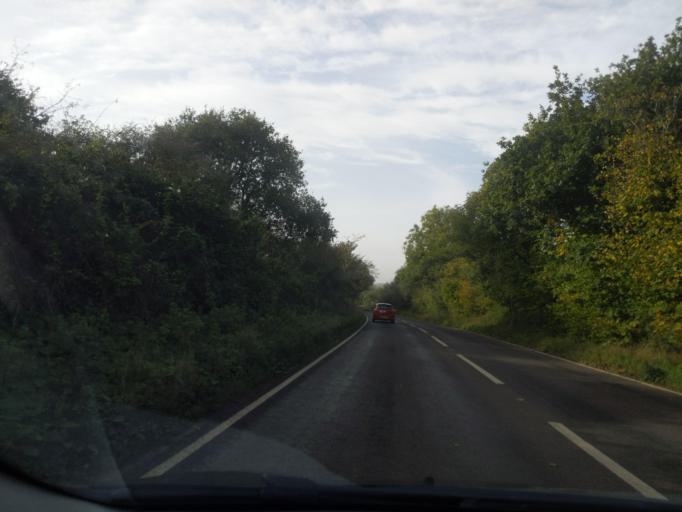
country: GB
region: England
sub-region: Cornwall
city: Saltash
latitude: 50.3740
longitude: -4.2599
